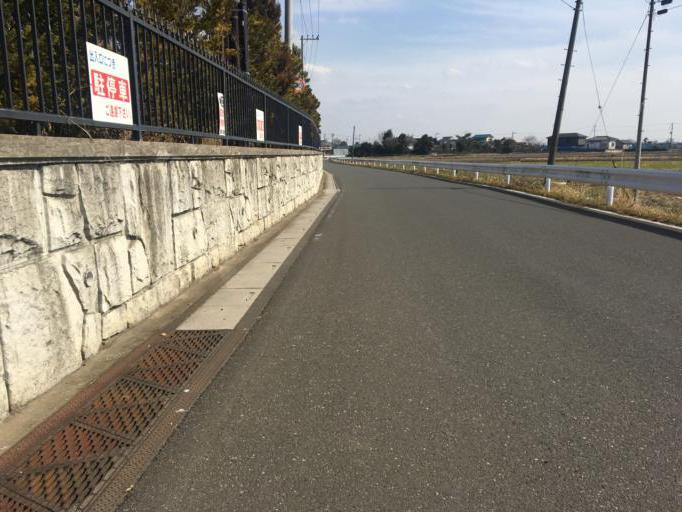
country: JP
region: Saitama
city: Shiki
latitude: 35.8721
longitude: 139.5614
